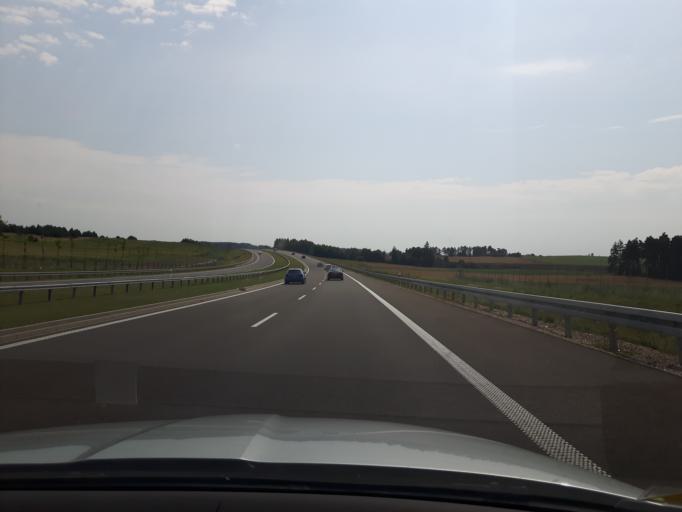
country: PL
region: Warmian-Masurian Voivodeship
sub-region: Powiat nidzicki
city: Nidzica
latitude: 53.3529
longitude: 20.3912
